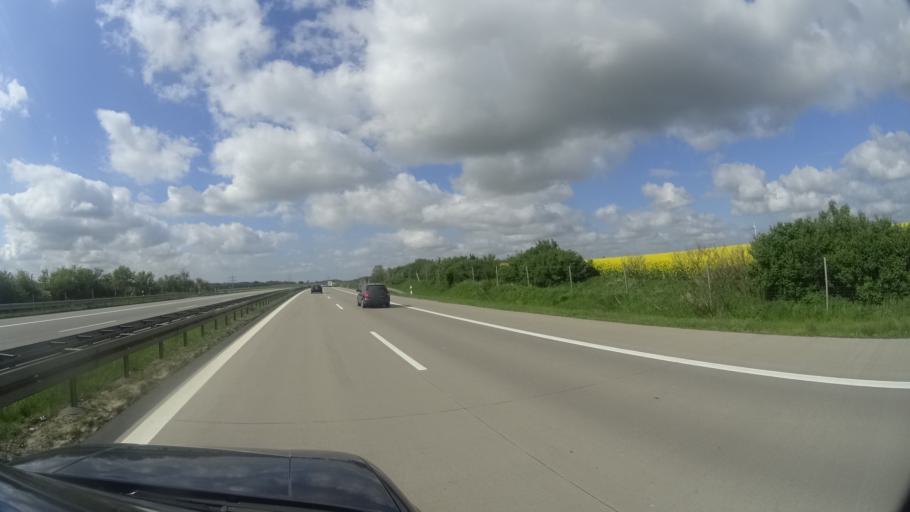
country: DE
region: Mecklenburg-Vorpommern
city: Kavelstorf
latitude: 53.9484
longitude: 12.2021
